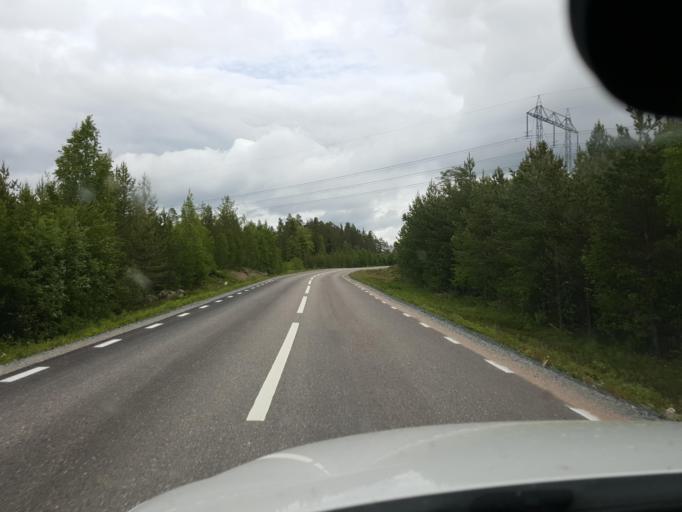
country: SE
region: Gaevleborg
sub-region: Ljusdals Kommun
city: Farila
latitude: 61.7581
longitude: 15.3857
